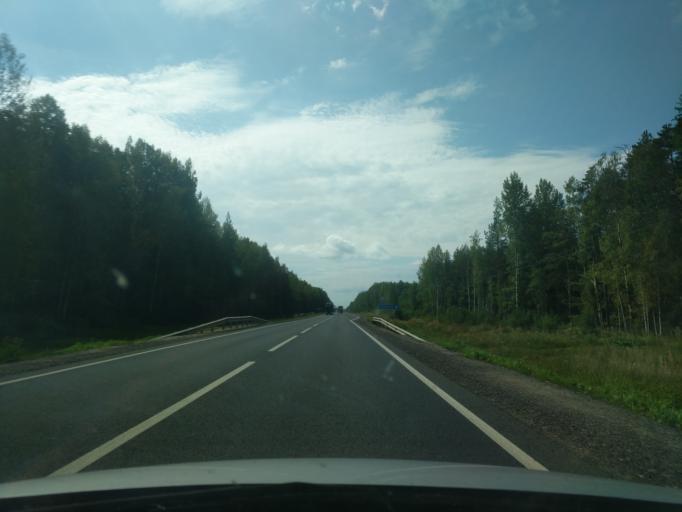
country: RU
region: Kostroma
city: Kadyy
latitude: 57.8171
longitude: 43.2359
